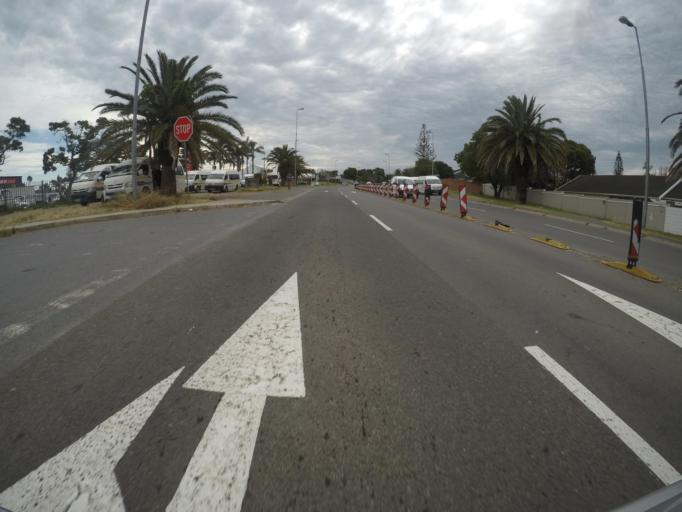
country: ZA
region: Eastern Cape
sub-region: Buffalo City Metropolitan Municipality
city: East London
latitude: -32.9664
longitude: 27.9400
